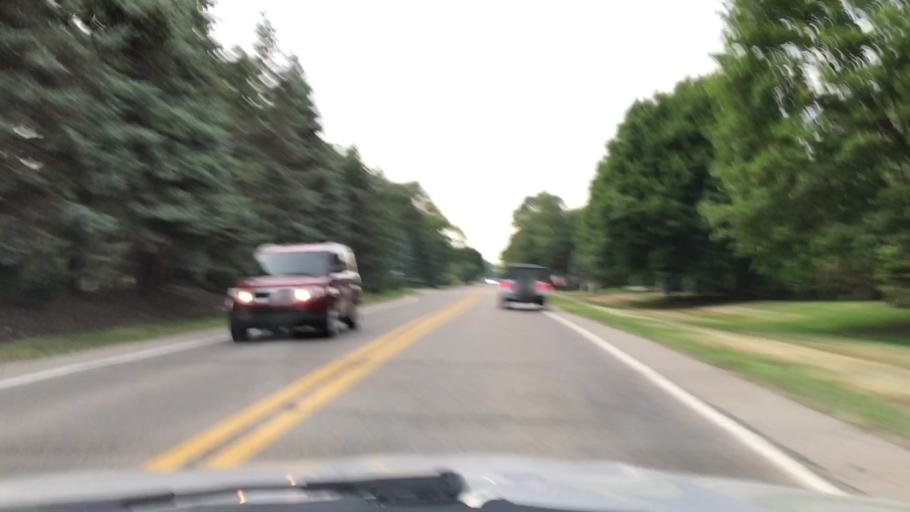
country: US
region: Michigan
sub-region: Wayne County
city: Northville
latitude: 42.4199
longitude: -83.5115
